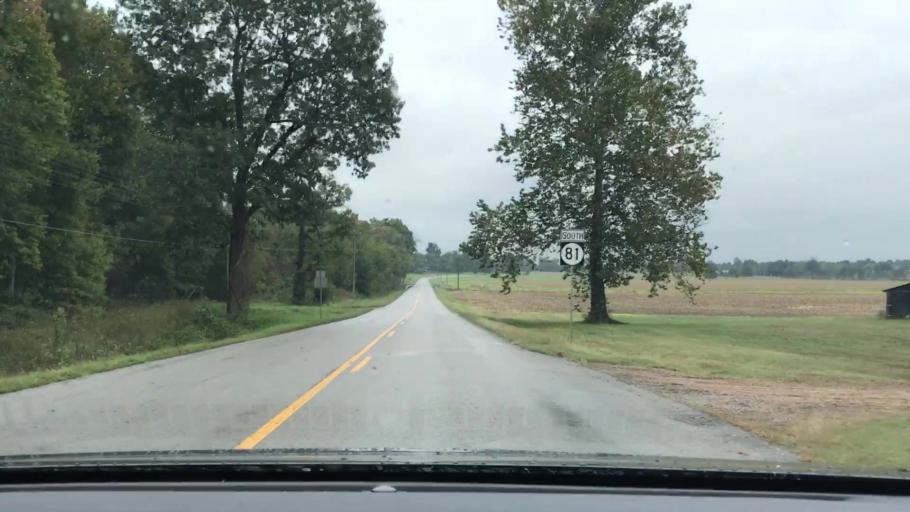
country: US
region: Kentucky
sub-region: McLean County
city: Calhoun
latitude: 37.4733
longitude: -87.2403
